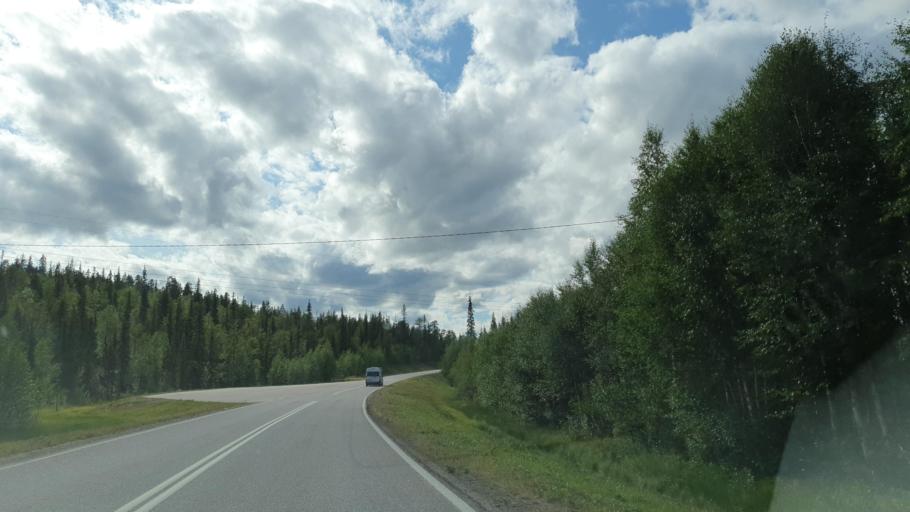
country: FI
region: Lapland
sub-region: Tunturi-Lappi
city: Muonio
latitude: 67.8665
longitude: 24.1700
